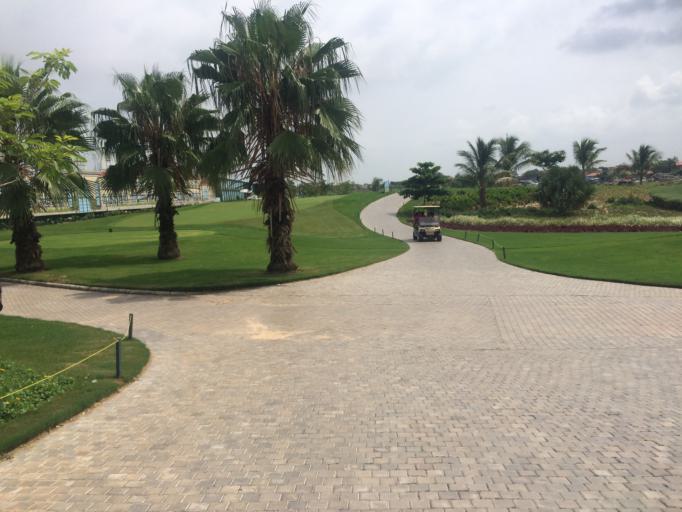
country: IN
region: Gujarat
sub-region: Ahmadabad
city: Sanand
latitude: 23.0170
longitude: 72.3576
